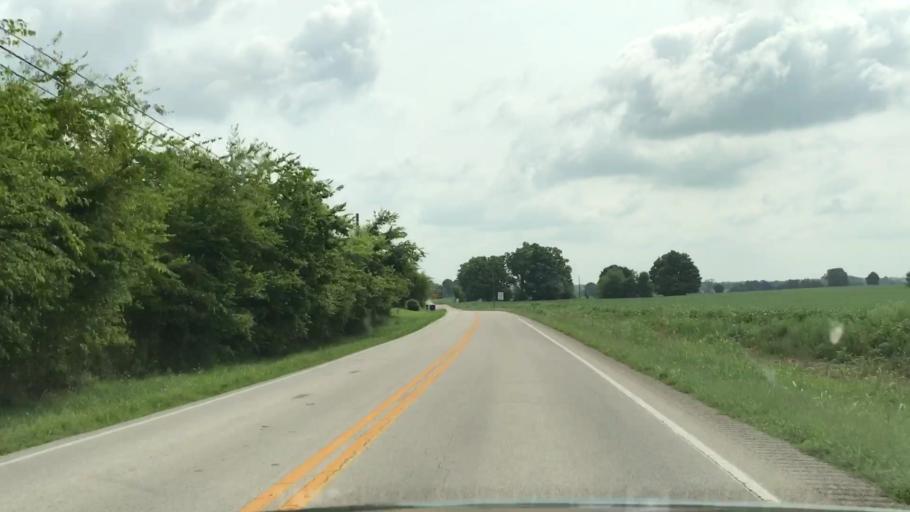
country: US
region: Kentucky
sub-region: Barren County
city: Cave City
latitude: 37.0922
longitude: -86.0968
